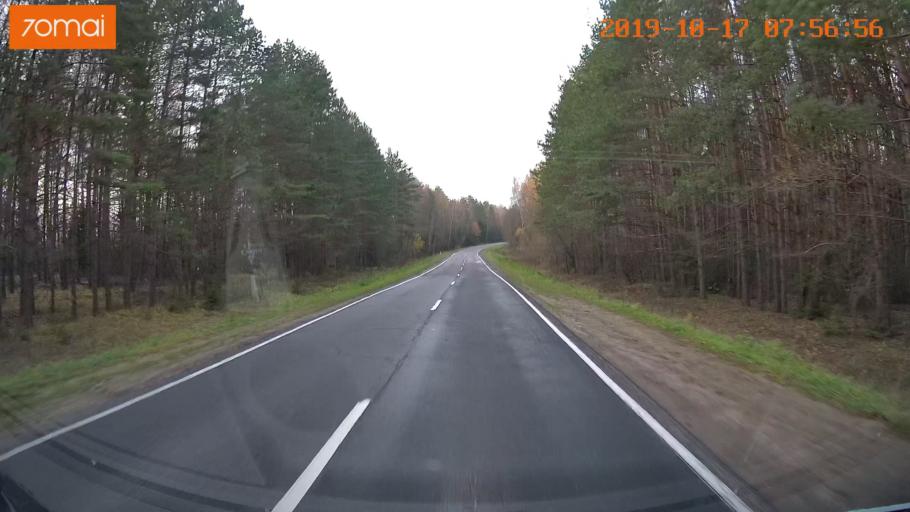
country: RU
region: Vladimir
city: Bavleny
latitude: 56.4169
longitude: 39.5844
